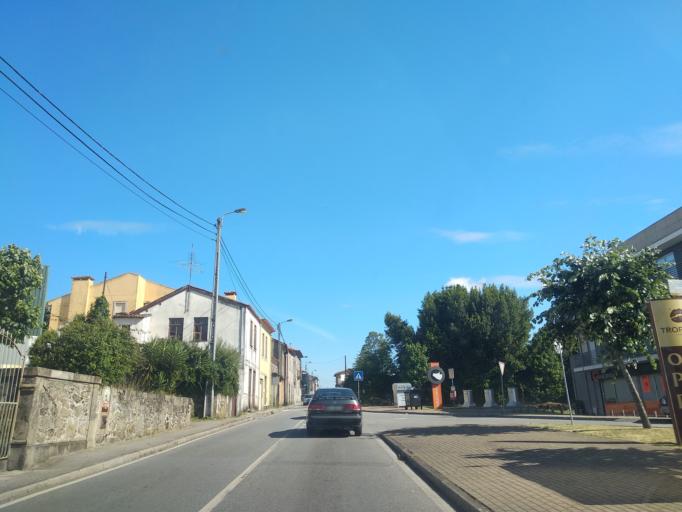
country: PT
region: Braga
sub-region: Vila Verde
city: Prado
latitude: 41.5860
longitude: -8.4558
